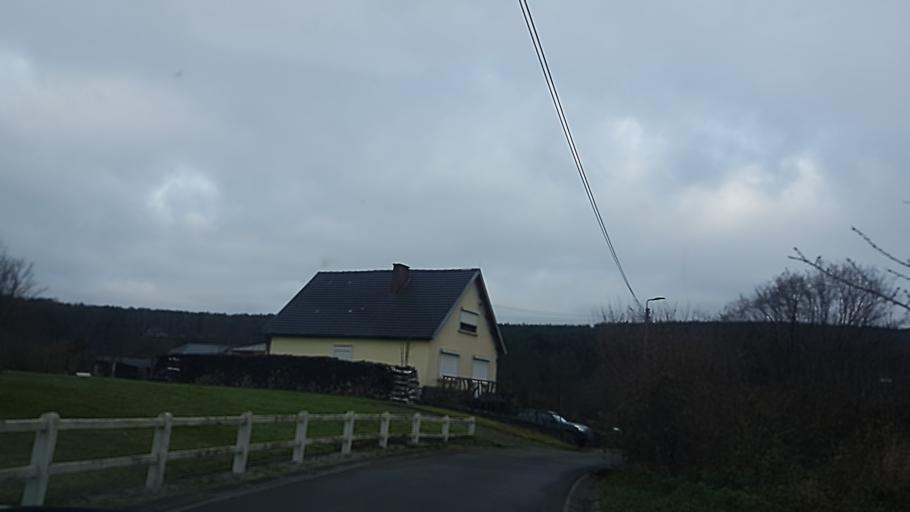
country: FR
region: Champagne-Ardenne
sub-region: Departement des Ardennes
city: Vireux-Molhain
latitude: 50.0729
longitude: 4.6103
